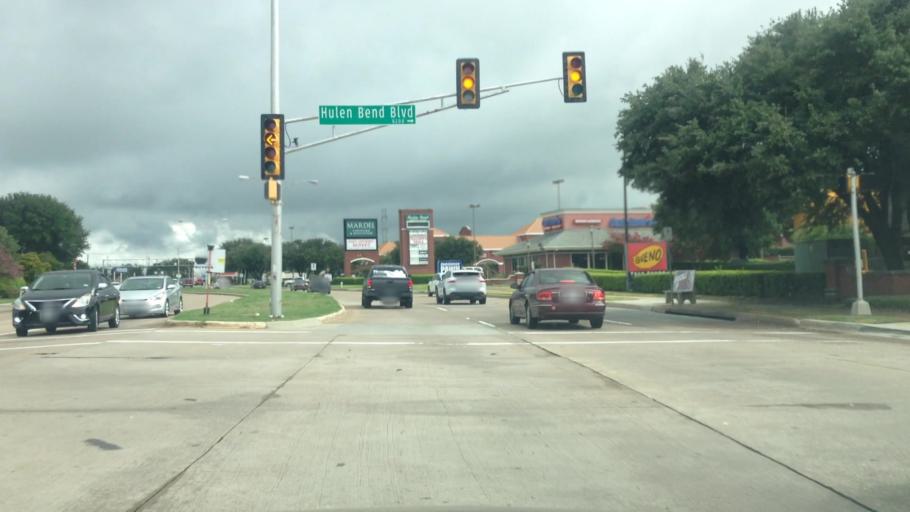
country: US
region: Texas
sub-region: Tarrant County
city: Edgecliff Village
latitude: 32.6614
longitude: -97.4020
